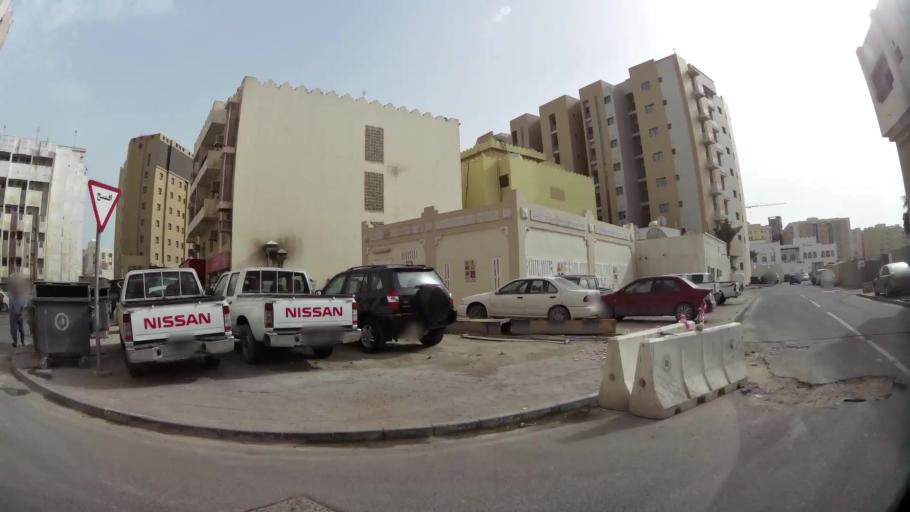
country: QA
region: Baladiyat ad Dawhah
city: Doha
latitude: 25.2794
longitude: 51.5474
